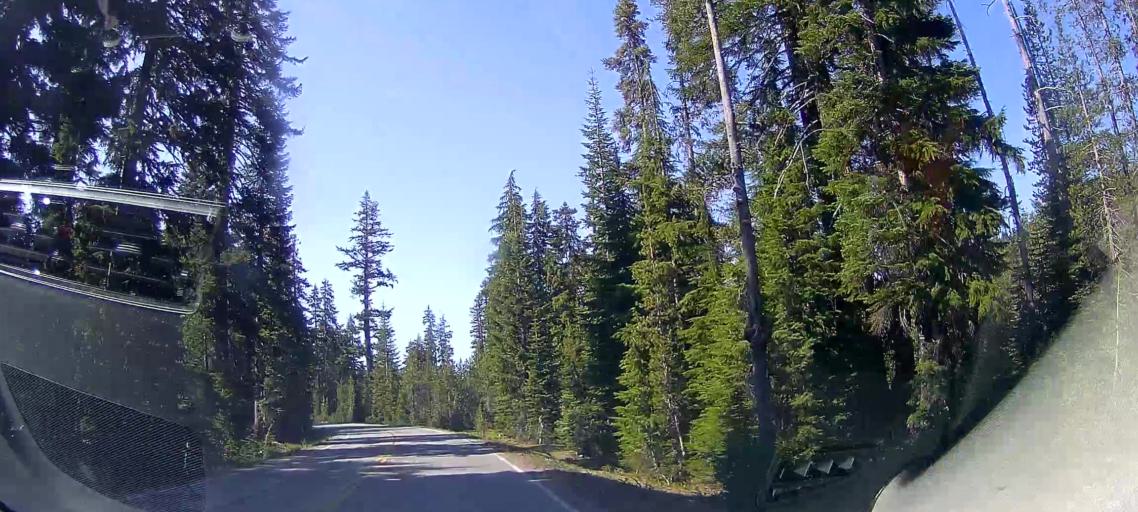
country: US
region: Oregon
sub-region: Jackson County
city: Shady Cove
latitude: 42.8947
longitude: -122.1343
